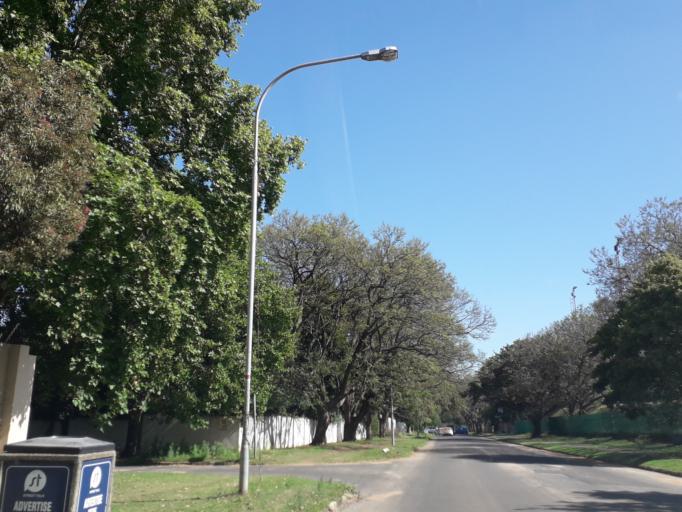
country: ZA
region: Gauteng
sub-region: City of Johannesburg Metropolitan Municipality
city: Johannesburg
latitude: -26.1574
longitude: 28.0618
